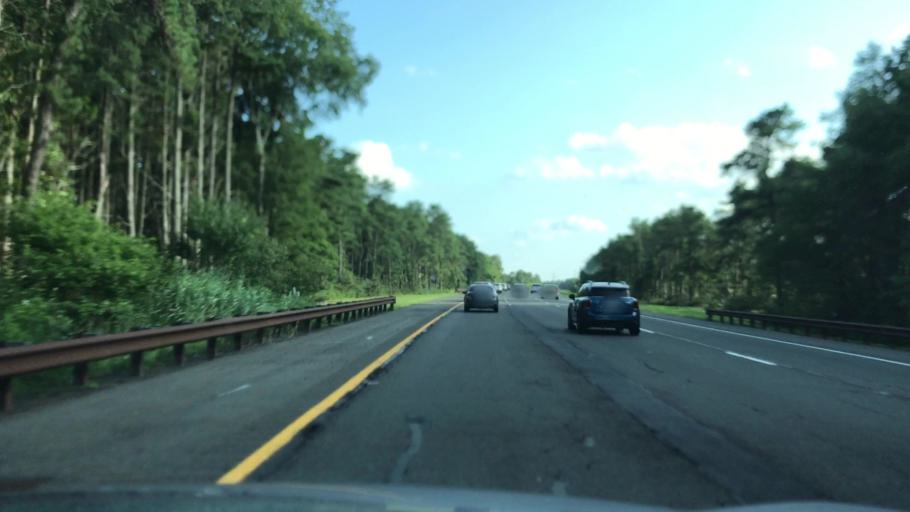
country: US
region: New Jersey
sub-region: Ocean County
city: Forked River
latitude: 39.8366
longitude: -74.2250
